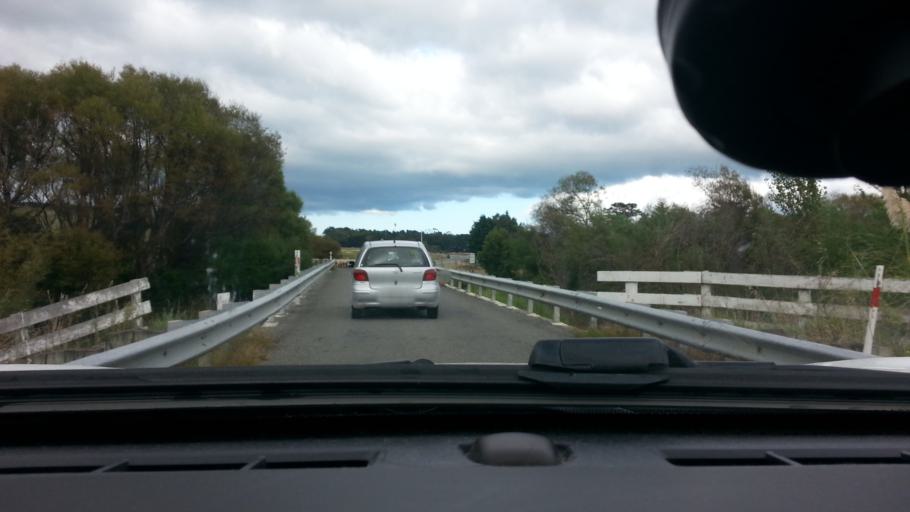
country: NZ
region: Wellington
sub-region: Upper Hutt City
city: Upper Hutt
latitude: -41.3691
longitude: 175.1811
